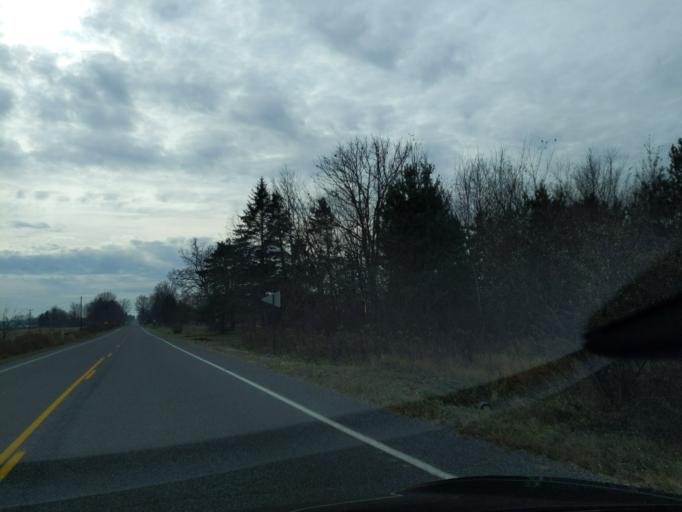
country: US
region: Michigan
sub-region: Ingham County
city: Mason
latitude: 42.5440
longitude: -84.5225
